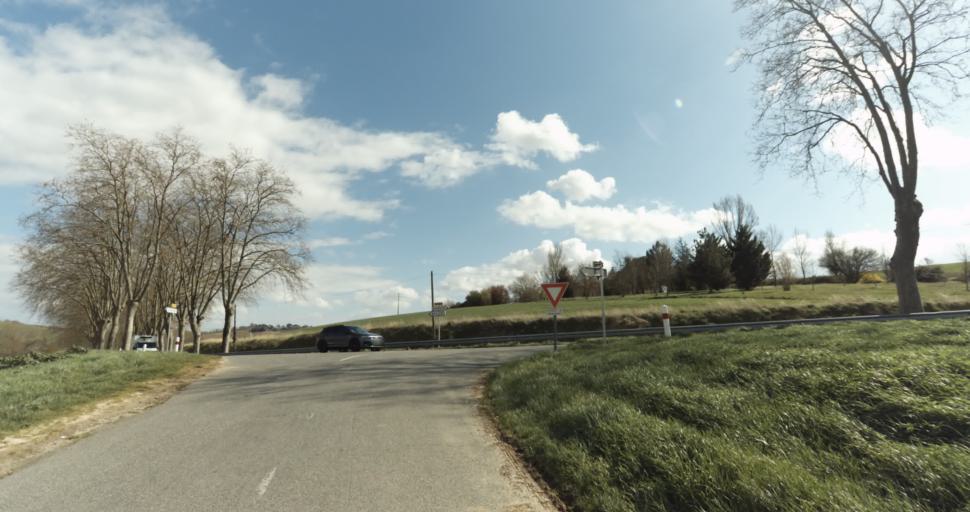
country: FR
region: Midi-Pyrenees
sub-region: Departement de la Haute-Garonne
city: Cintegabelle
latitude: 43.3634
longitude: 1.5283
